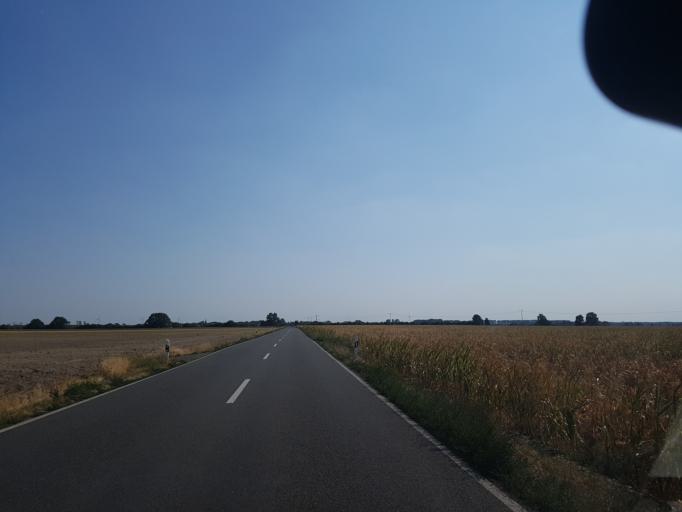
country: DE
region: Saxony-Anhalt
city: Annaburg
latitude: 51.6898
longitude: 12.9976
